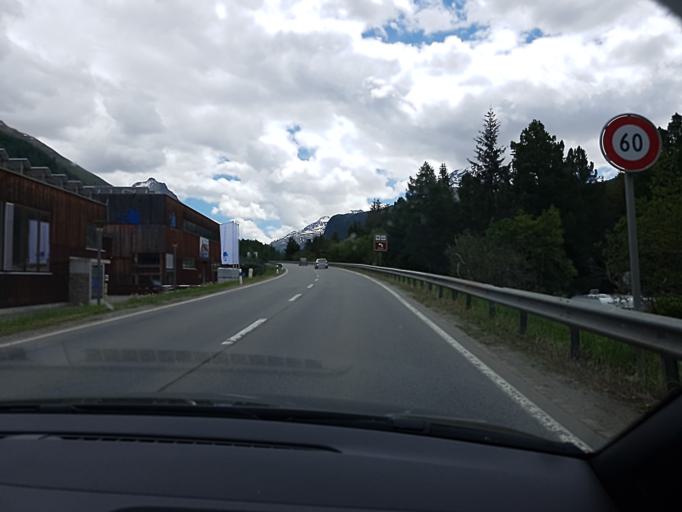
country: CH
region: Grisons
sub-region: Maloja District
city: Celerina
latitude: 46.5104
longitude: 9.8796
